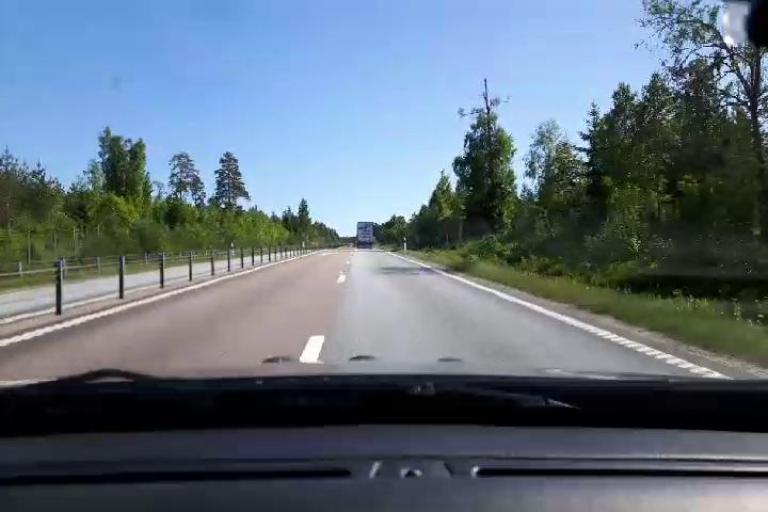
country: SE
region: Gaevleborg
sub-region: Soderhamns Kommun
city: Soderhamn
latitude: 61.2675
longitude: 17.0287
